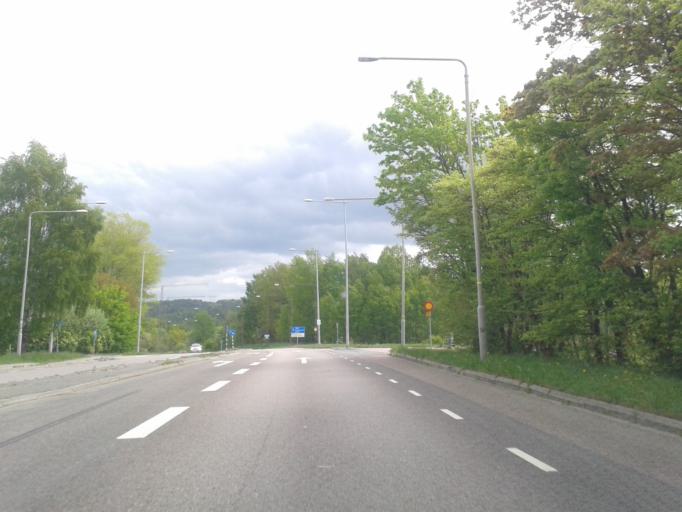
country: SE
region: Vaestra Goetaland
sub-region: Goteborg
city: Eriksbo
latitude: 57.7725
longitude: 12.0447
